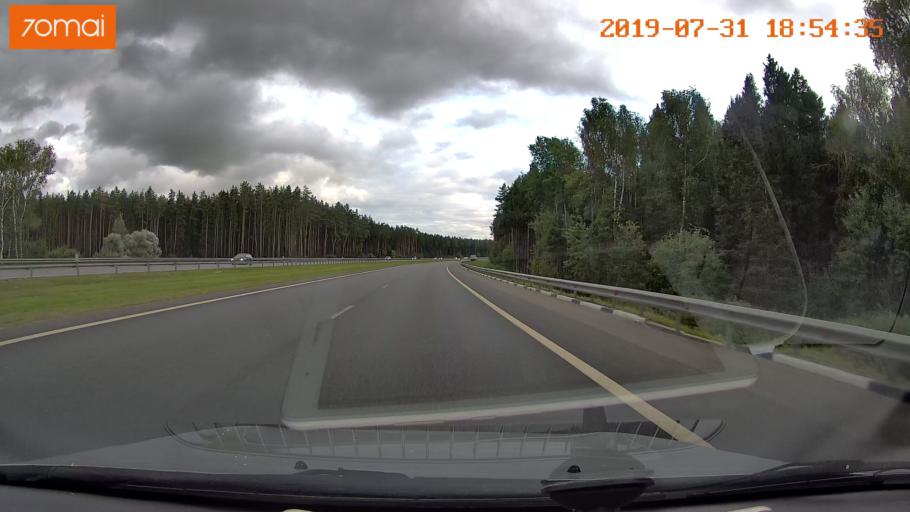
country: RU
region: Moskovskaya
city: Raduzhnyy
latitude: 55.1877
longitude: 38.6688
